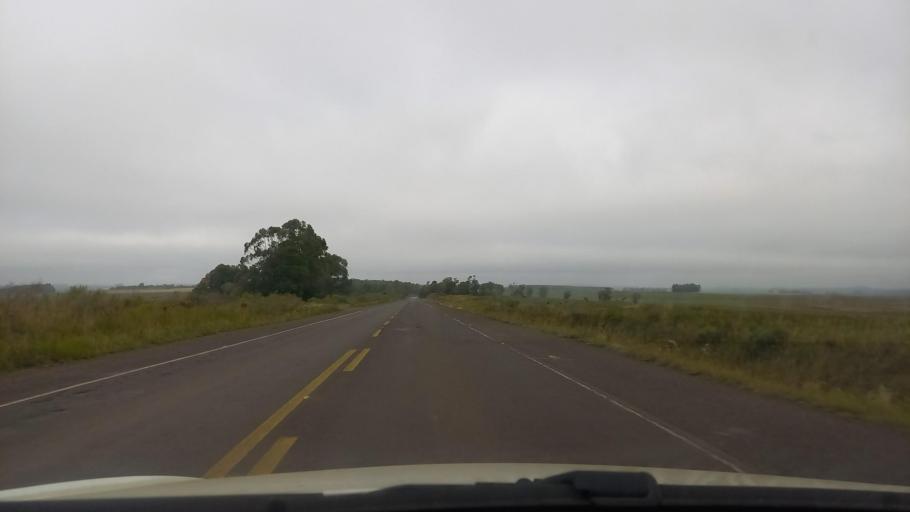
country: BR
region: Rio Grande do Sul
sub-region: Cacequi
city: Cacequi
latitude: -30.0558
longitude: -54.6032
